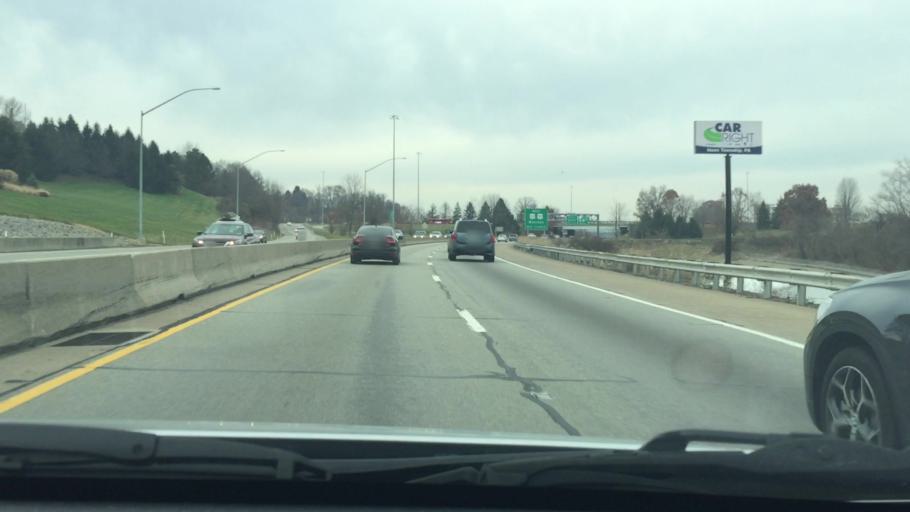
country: US
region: Pennsylvania
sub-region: Allegheny County
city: Rennerdale
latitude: 40.4442
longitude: -80.1630
